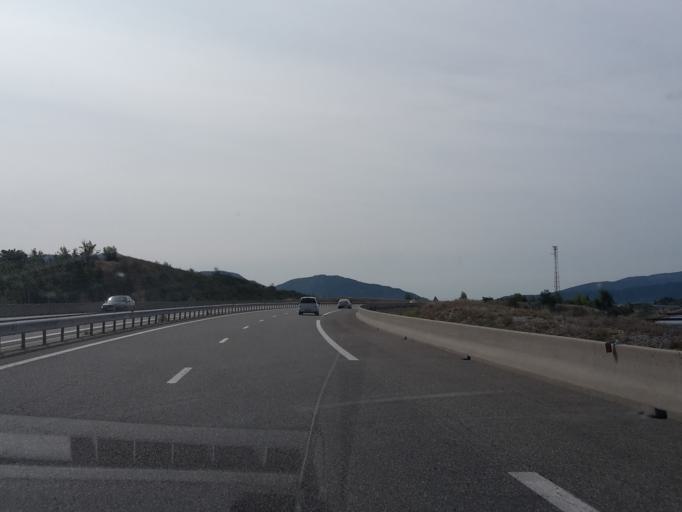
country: FR
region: Provence-Alpes-Cote d'Azur
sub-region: Departement des Hautes-Alpes
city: Laragne-Monteglin
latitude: 44.3109
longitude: 5.8991
